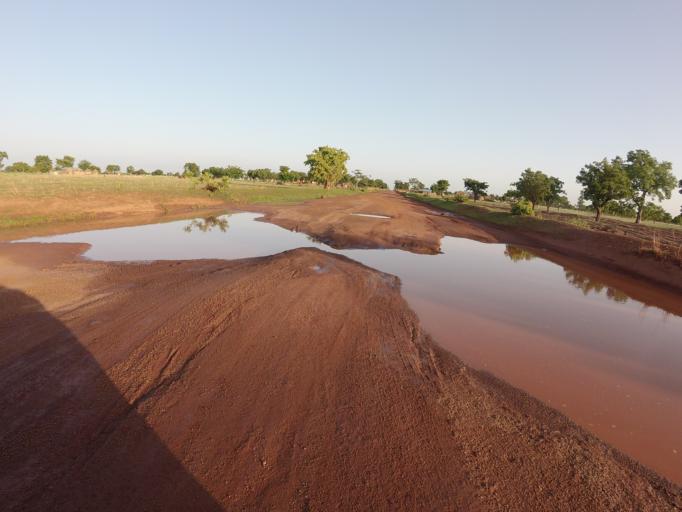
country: TG
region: Savanes
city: Sansanne-Mango
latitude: 10.2687
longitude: -0.0813
